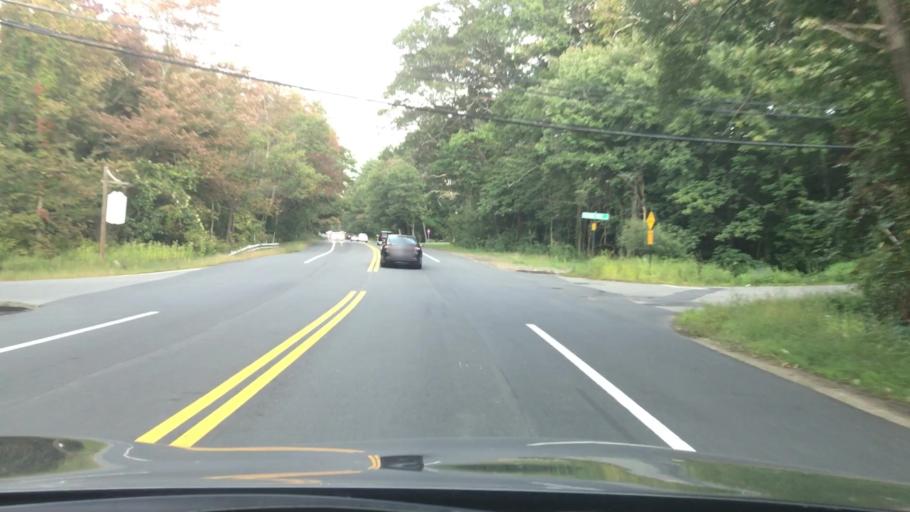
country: US
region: Massachusetts
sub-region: Middlesex County
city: Weston
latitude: 42.3639
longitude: -71.3103
